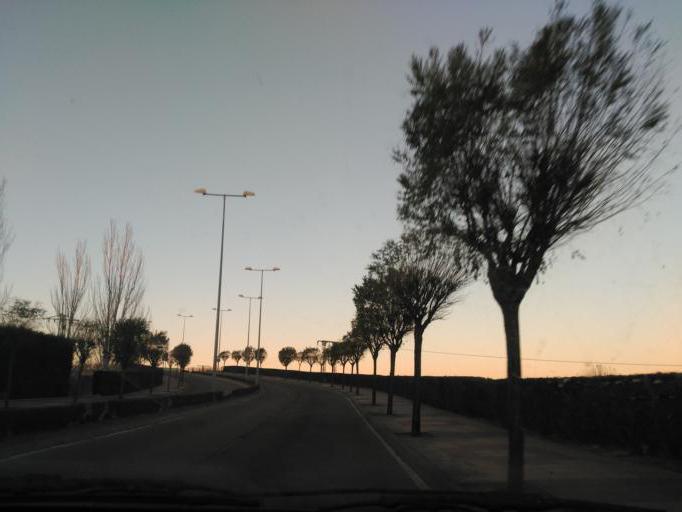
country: ES
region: Castille and Leon
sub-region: Provincia de Salamanca
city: Carbajosa de la Sagrada
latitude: 40.9365
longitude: -5.6518
